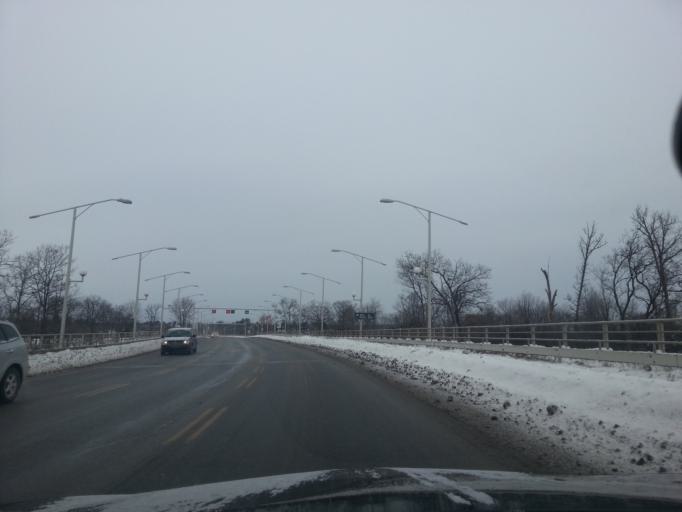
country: CA
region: Ontario
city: Ottawa
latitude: 45.4065
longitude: -75.7553
